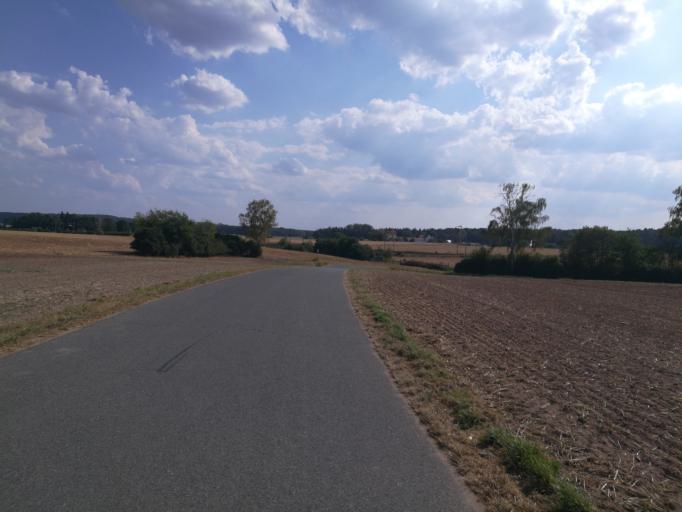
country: DE
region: Bavaria
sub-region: Regierungsbezirk Mittelfranken
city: Veitsbronn
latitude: 49.5023
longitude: 10.9019
